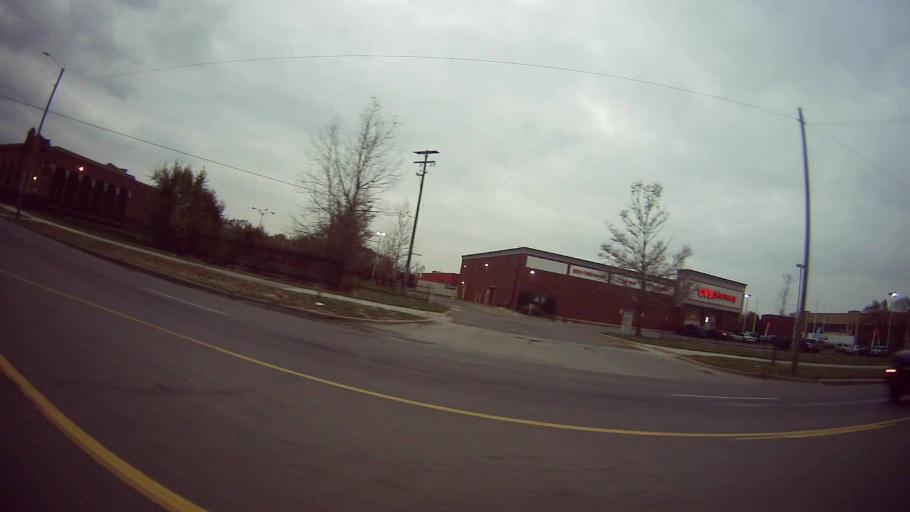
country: US
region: Michigan
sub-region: Wayne County
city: Hamtramck
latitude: 42.4043
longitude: -82.9966
